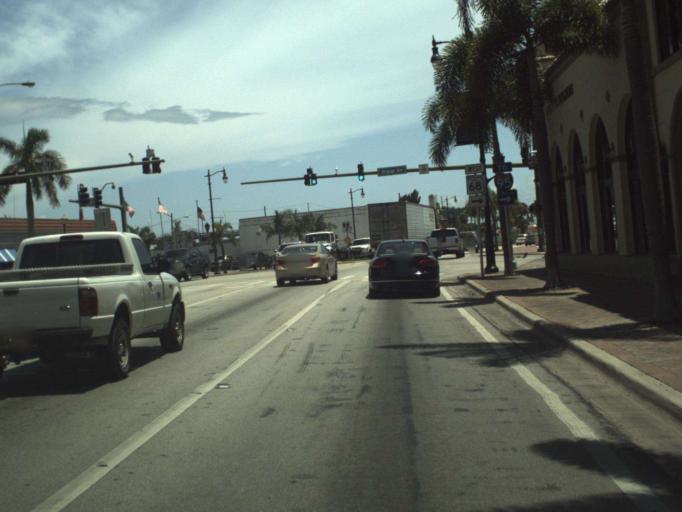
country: US
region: Florida
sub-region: Saint Lucie County
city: Fort Pierce
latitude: 27.4474
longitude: -80.3262
